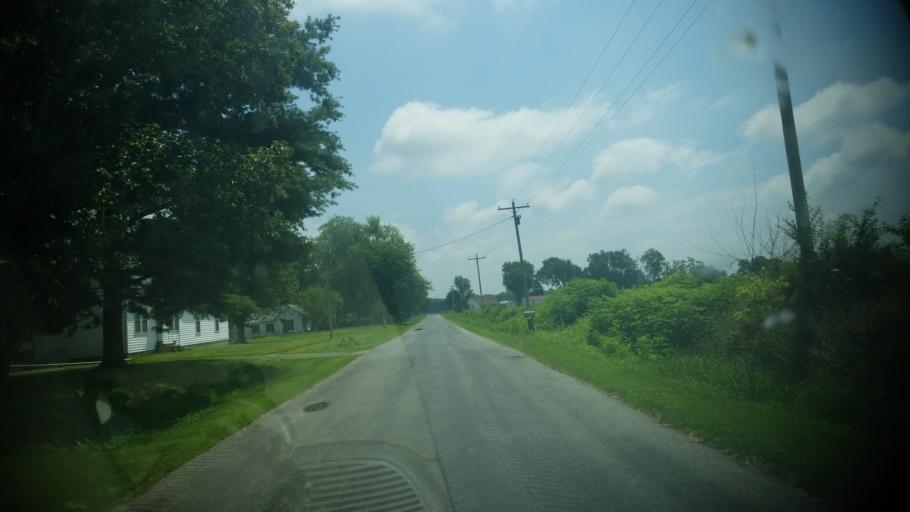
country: US
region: Illinois
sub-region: Wayne County
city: Fairfield
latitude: 38.5223
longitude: -88.3532
